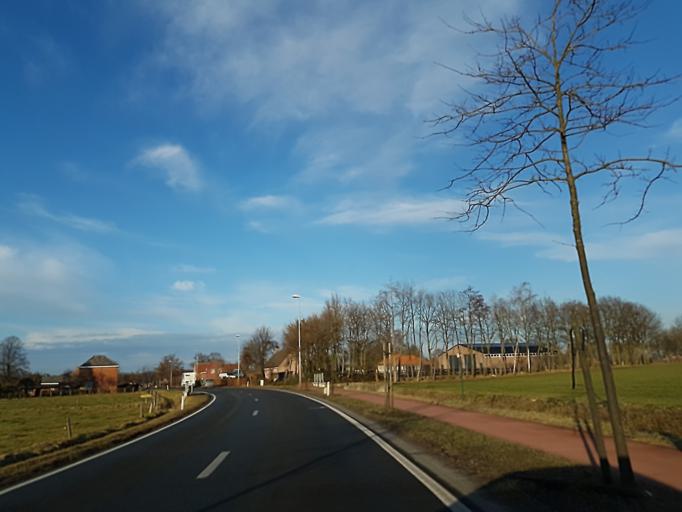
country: BE
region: Flanders
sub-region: Provincie Antwerpen
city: Ravels
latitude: 51.3840
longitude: 4.9947
